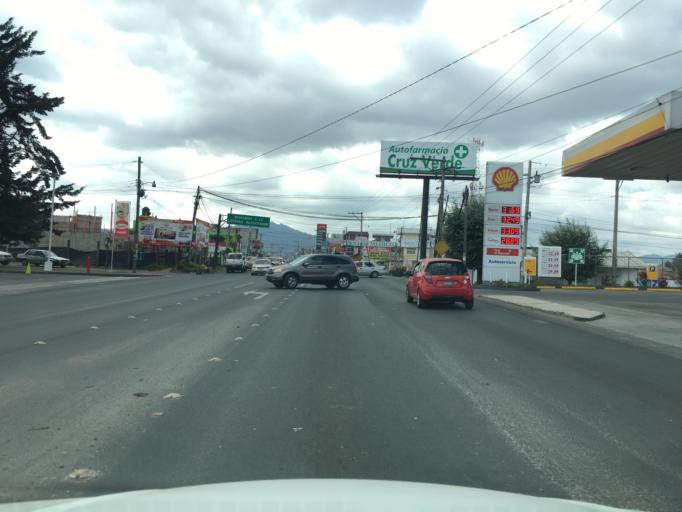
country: GT
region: Quetzaltenango
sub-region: Municipio de La Esperanza
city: La Esperanza
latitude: 14.8654
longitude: -91.5621
